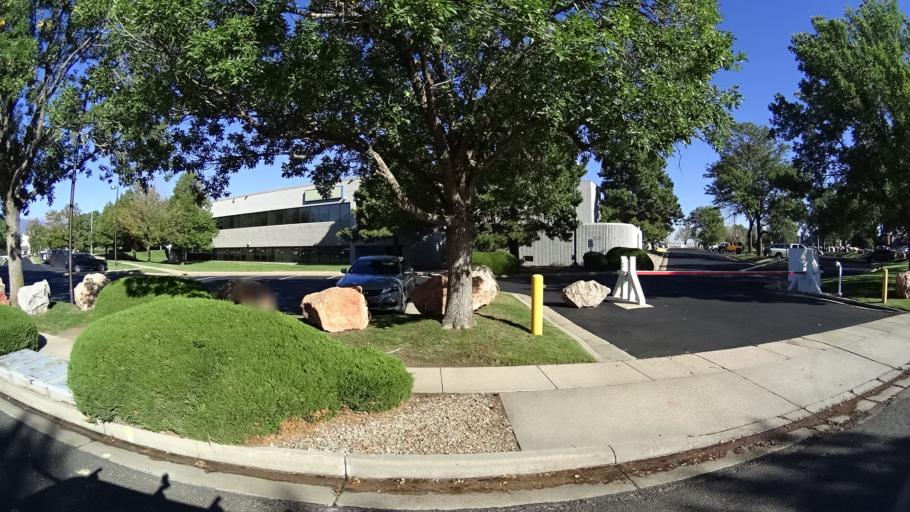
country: US
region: Colorado
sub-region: El Paso County
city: Cimarron Hills
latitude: 38.8084
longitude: -104.7257
